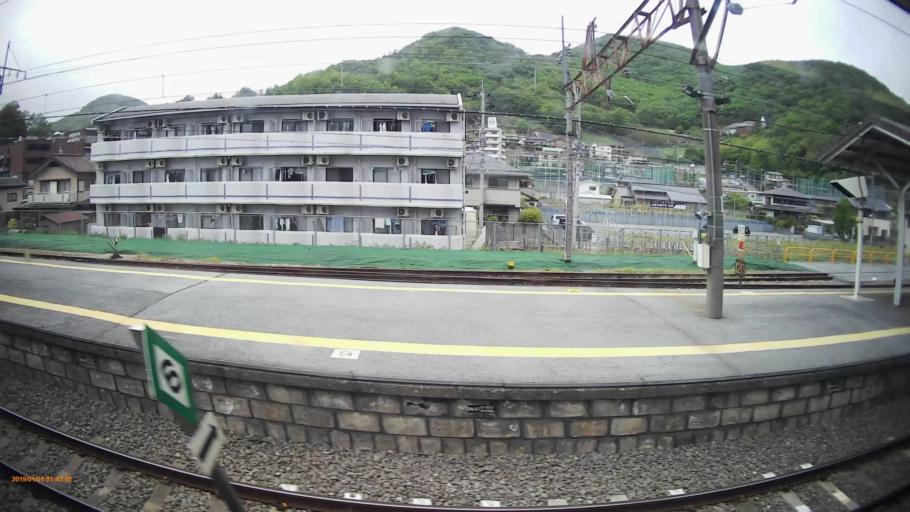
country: JP
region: Yamanashi
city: Kofu-shi
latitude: 35.6599
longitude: 138.5982
